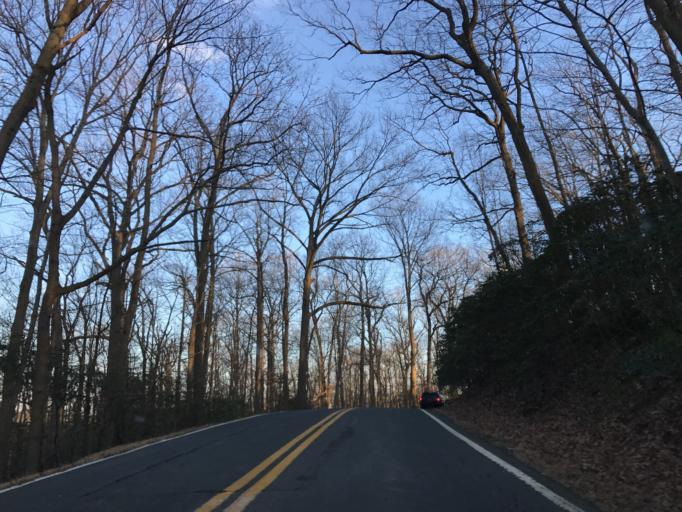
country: US
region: Maryland
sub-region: Cecil County
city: Charlestown
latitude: 39.4796
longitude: -75.9843
